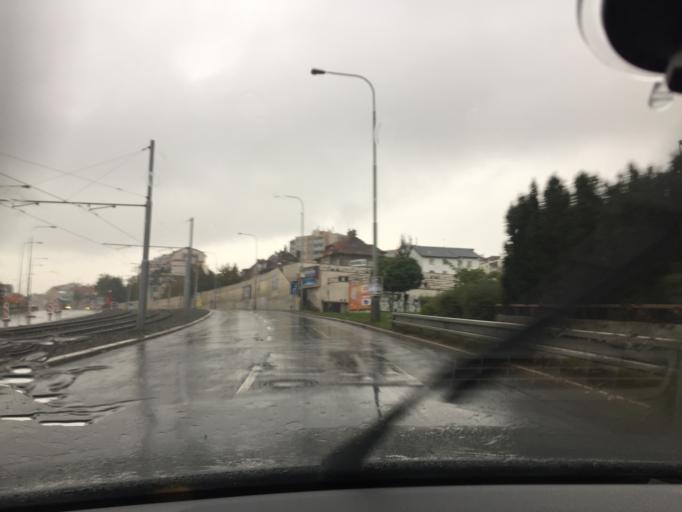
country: CZ
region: Praha
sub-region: Praha 8
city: Liben
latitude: 50.1186
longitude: 14.4661
